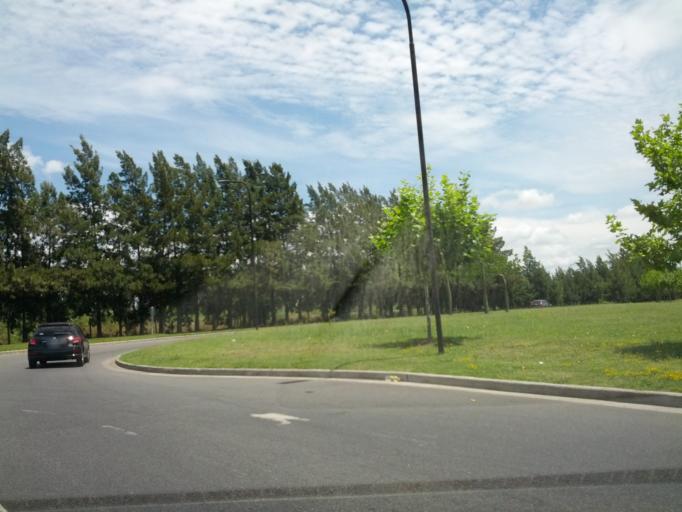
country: AR
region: Buenos Aires
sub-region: Partido de Tigre
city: Tigre
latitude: -34.4418
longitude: -58.6402
